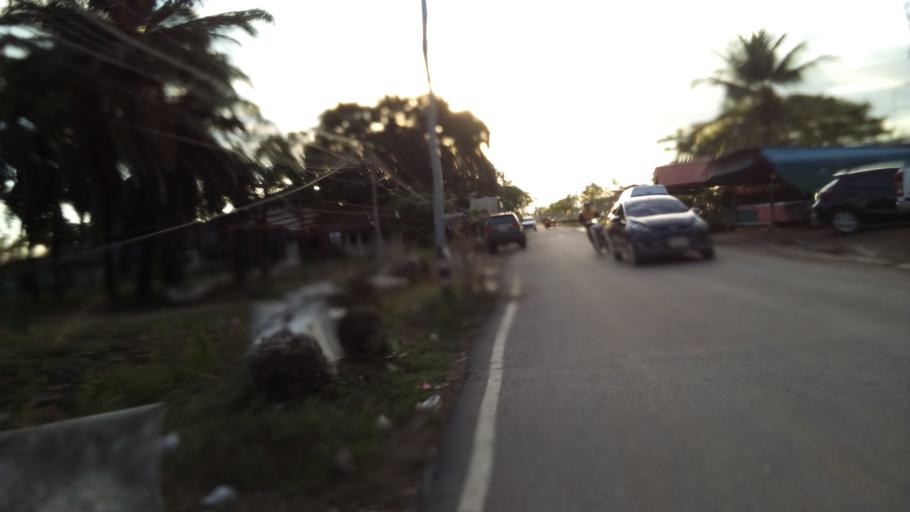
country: TH
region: Pathum Thani
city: Nong Suea
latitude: 14.0731
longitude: 100.8844
